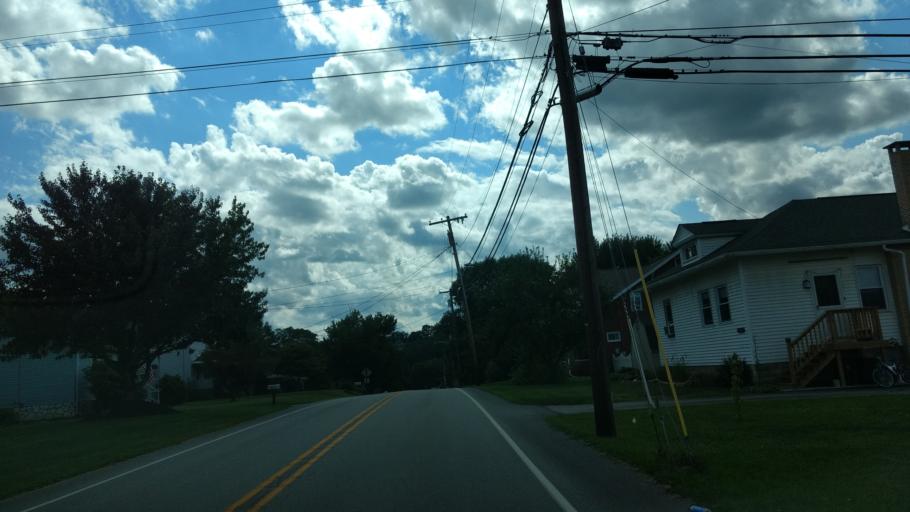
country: US
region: Pennsylvania
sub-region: Armstrong County
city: Apollo
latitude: 40.5757
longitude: -79.5709
